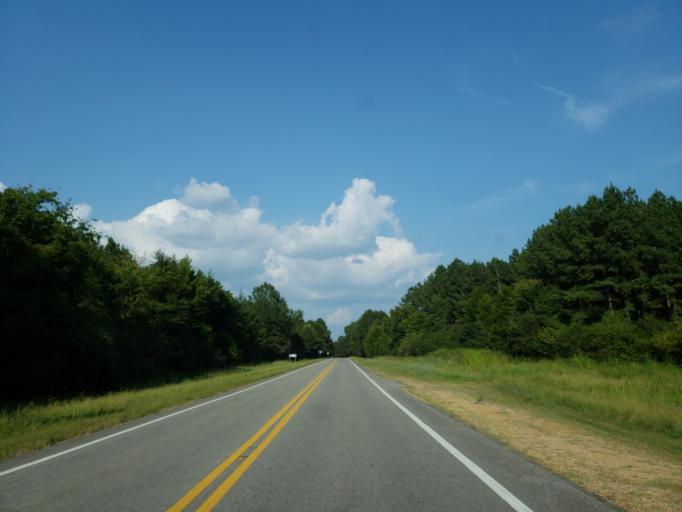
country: US
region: Alabama
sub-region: Greene County
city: Eutaw
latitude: 32.7577
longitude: -88.0178
